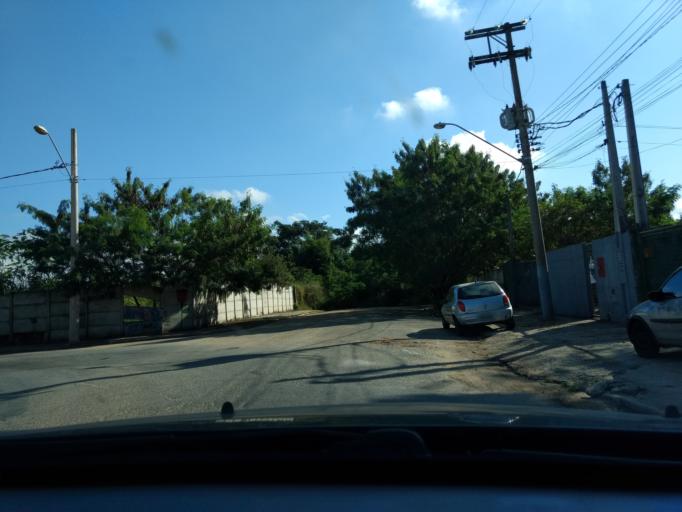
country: BR
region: Sao Paulo
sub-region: Taubate
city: Taubate
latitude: -23.0061
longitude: -45.5214
